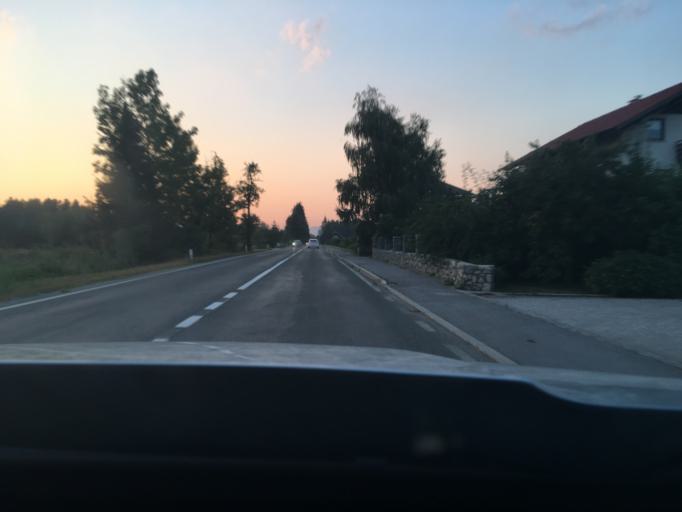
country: SI
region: Ribnica
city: Ribnica
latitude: 45.7240
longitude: 14.7409
